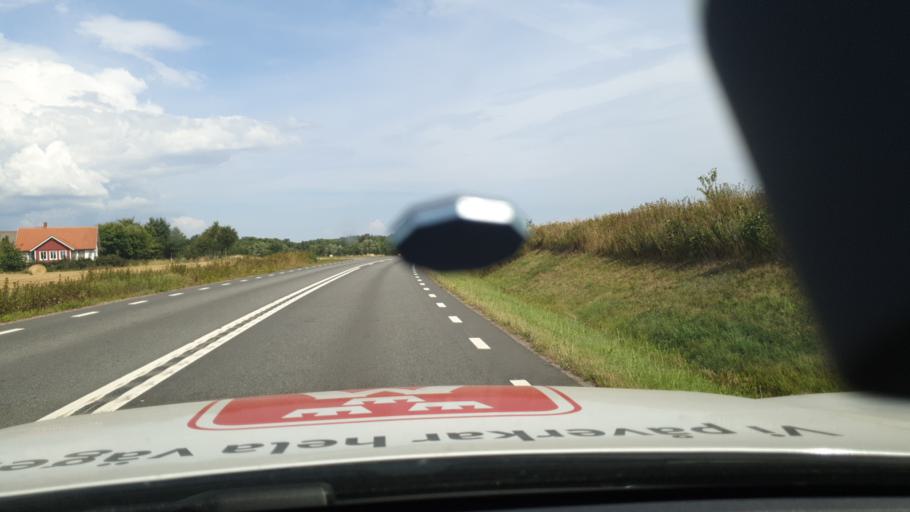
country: SE
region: Skane
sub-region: Simrishamns Kommun
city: Kivik
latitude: 55.5893
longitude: 14.1245
